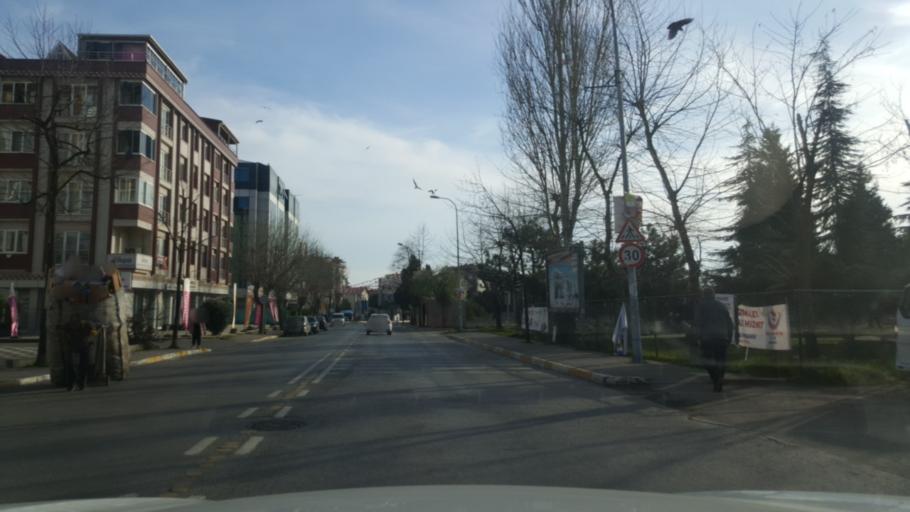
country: TR
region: Istanbul
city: Icmeler
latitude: 40.8231
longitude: 29.3098
